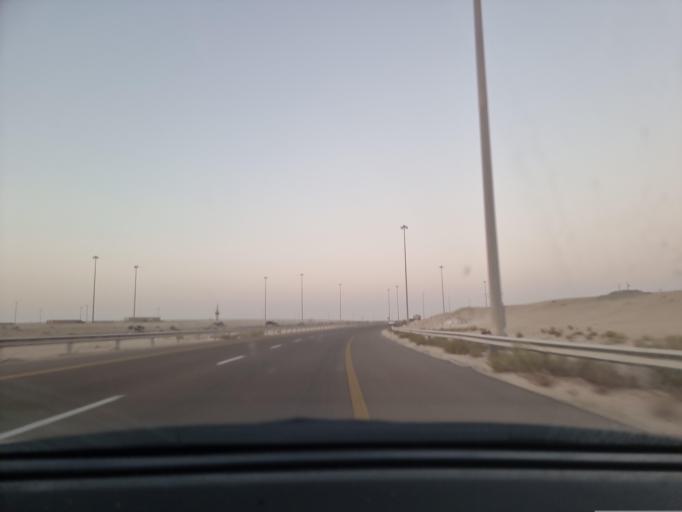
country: AE
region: Abu Dhabi
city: Abu Dhabi
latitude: 24.3794
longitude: 54.7353
